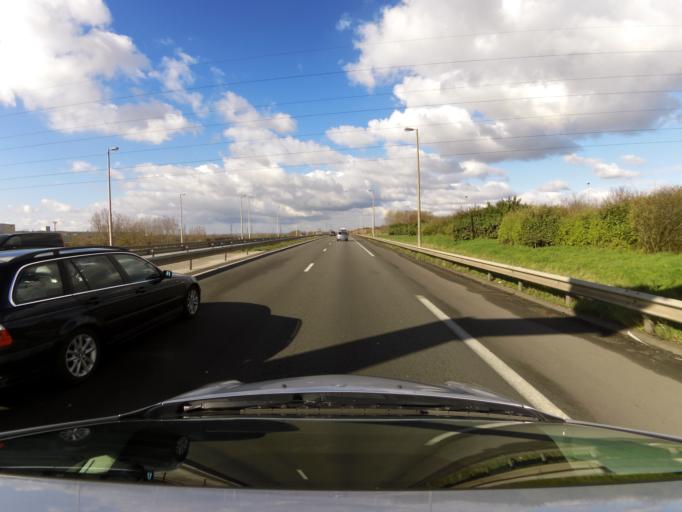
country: FR
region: Nord-Pas-de-Calais
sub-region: Departement du Nord
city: Grande-Synthe
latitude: 50.9988
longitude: 2.2891
